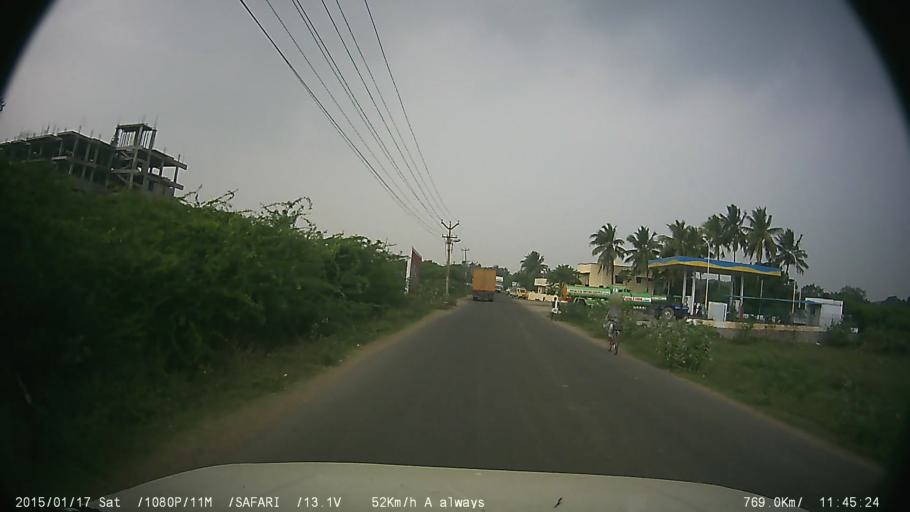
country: IN
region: Tamil Nadu
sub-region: Kancheepuram
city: Singapperumalkovil
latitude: 12.7667
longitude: 79.9976
